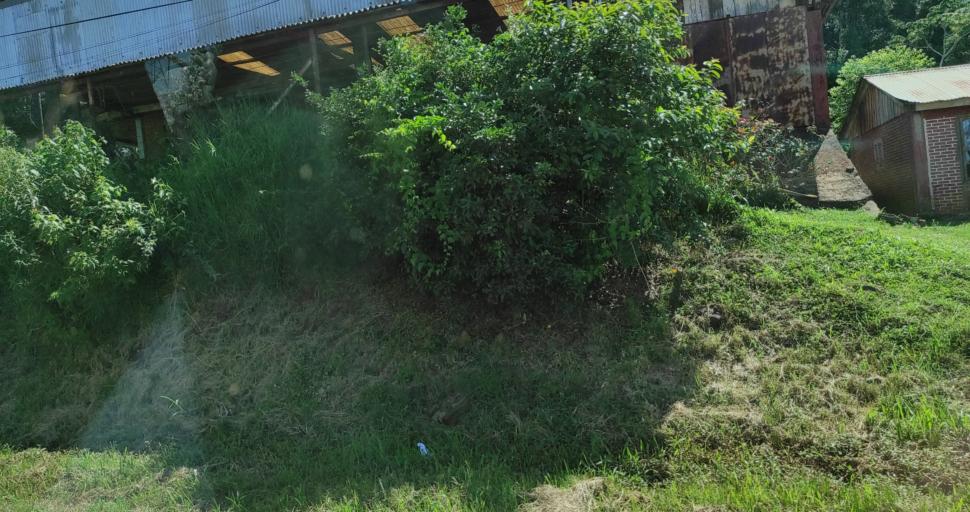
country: AR
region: Misiones
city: El Soberbio
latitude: -27.2878
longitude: -54.1987
